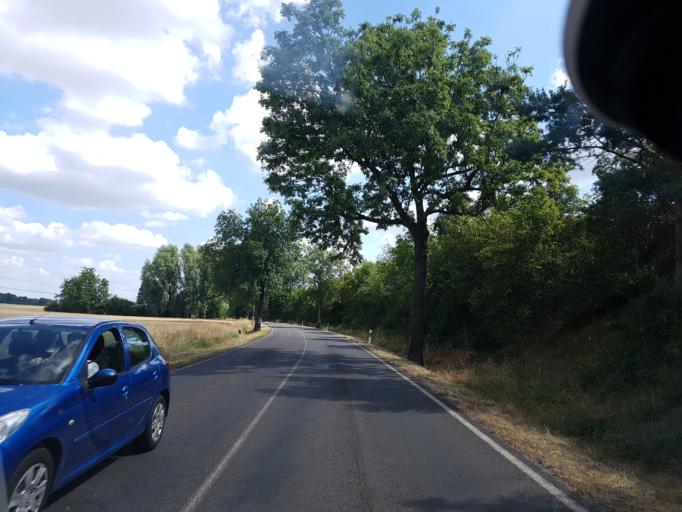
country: DE
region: Brandenburg
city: Drebkau
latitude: 51.6567
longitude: 14.2326
